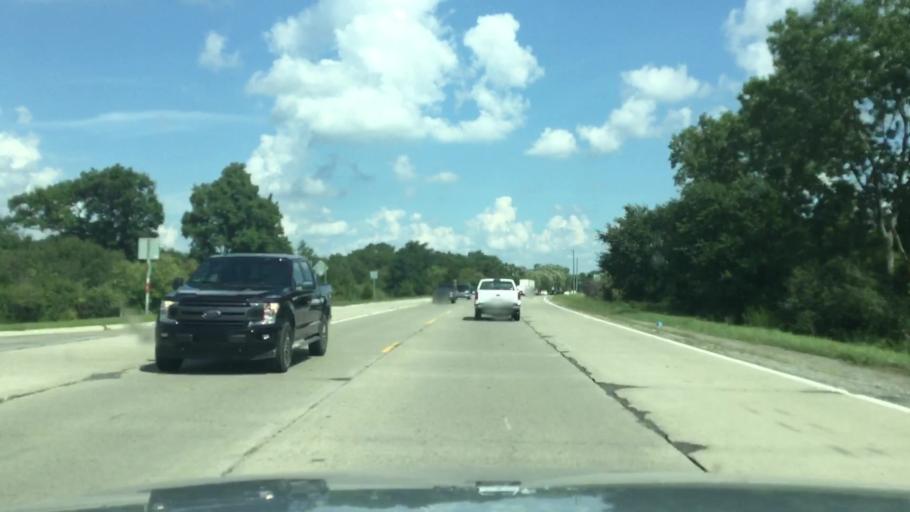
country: US
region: Michigan
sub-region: Washtenaw County
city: Saline
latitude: 42.1927
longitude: -83.7208
